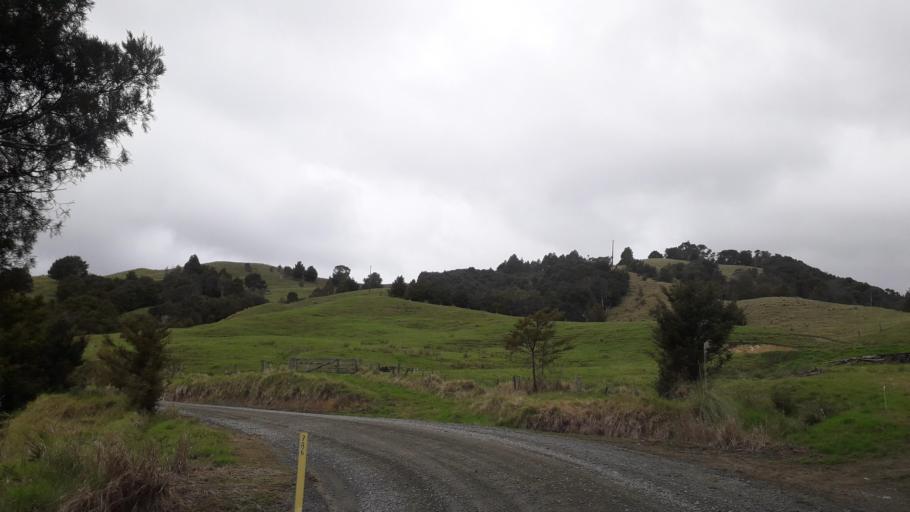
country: NZ
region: Northland
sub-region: Far North District
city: Kerikeri
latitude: -35.1307
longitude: 173.7200
